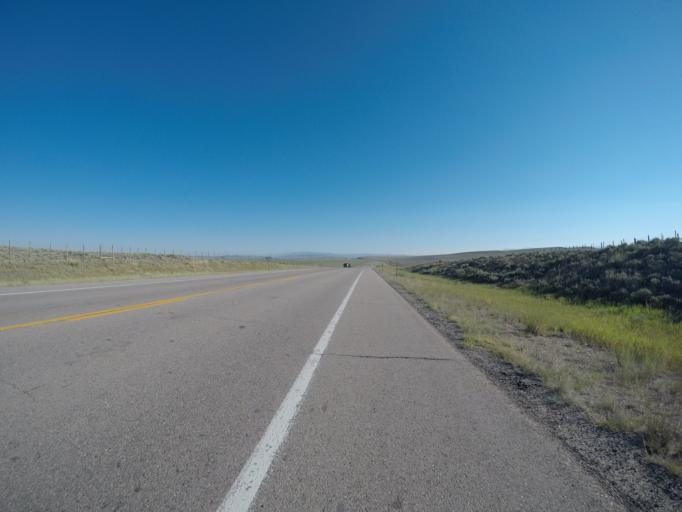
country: US
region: Wyoming
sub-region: Sublette County
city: Pinedale
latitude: 42.9226
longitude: -110.0806
